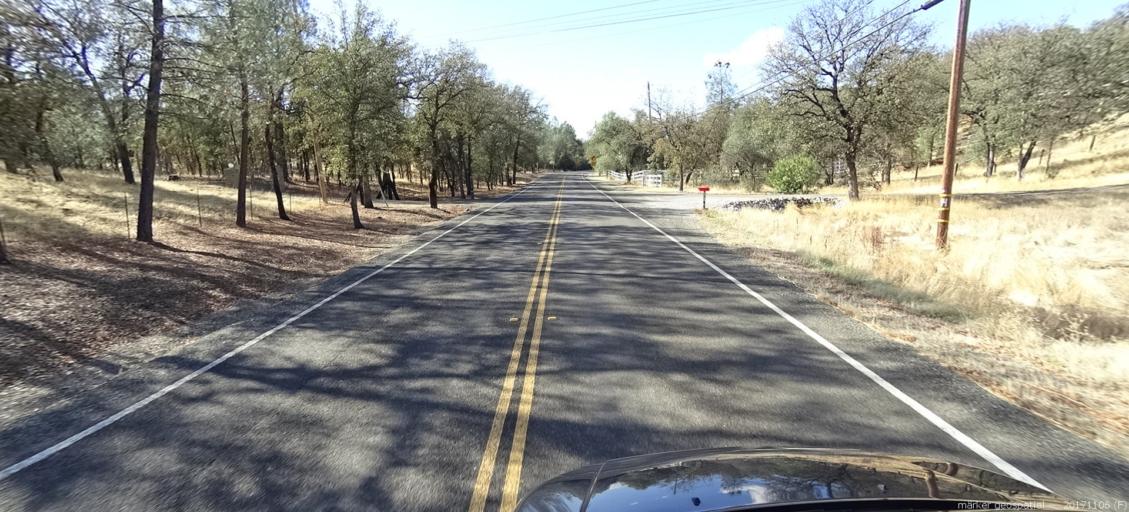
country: US
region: California
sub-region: Shasta County
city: Palo Cedro
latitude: 40.5916
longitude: -122.2755
